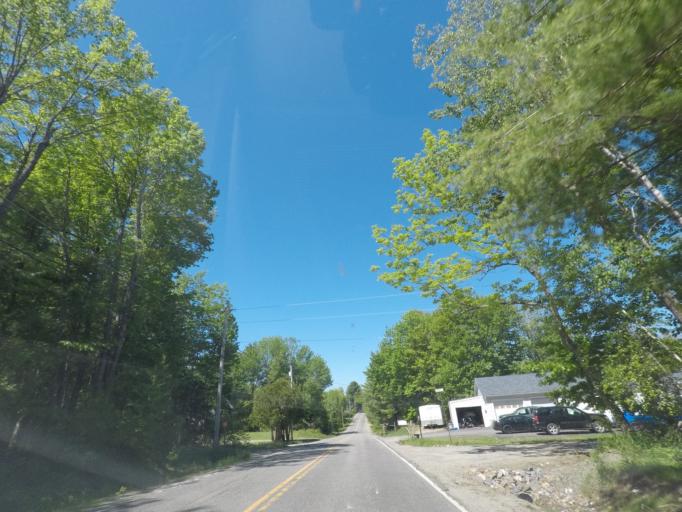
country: US
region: Maine
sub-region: Kennebec County
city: Gardiner
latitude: 44.2285
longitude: -69.8297
